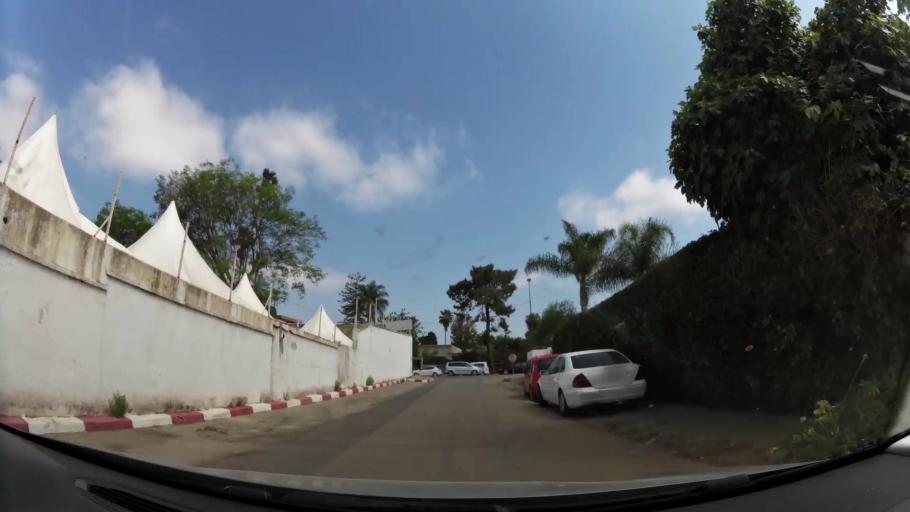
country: MA
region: Rabat-Sale-Zemmour-Zaer
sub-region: Rabat
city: Rabat
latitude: 33.9797
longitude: -6.8360
